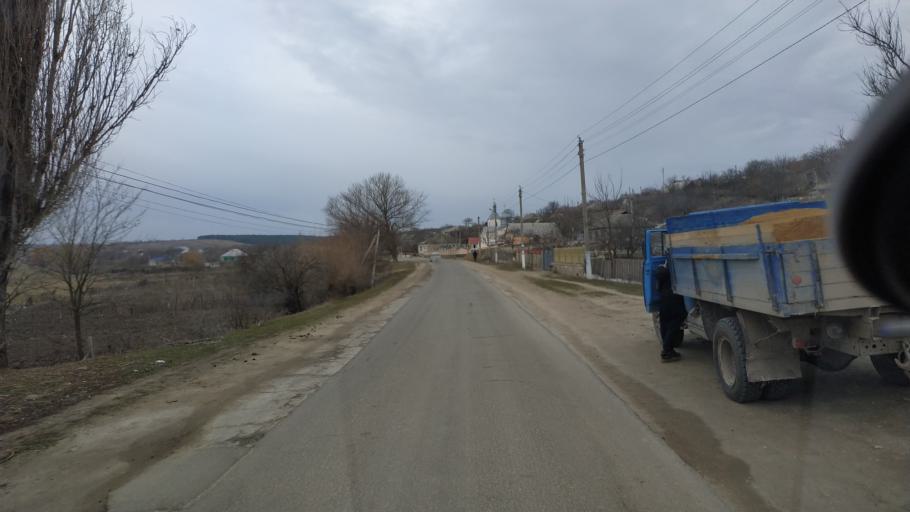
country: MD
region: Telenesti
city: Cocieri
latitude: 47.2674
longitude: 29.0707
